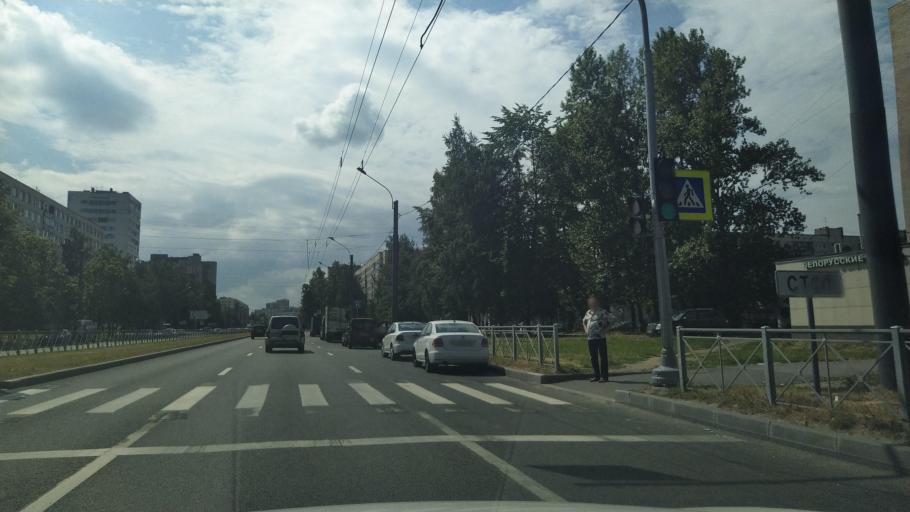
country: RU
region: Leningrad
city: Parnas
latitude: 60.0452
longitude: 30.3510
